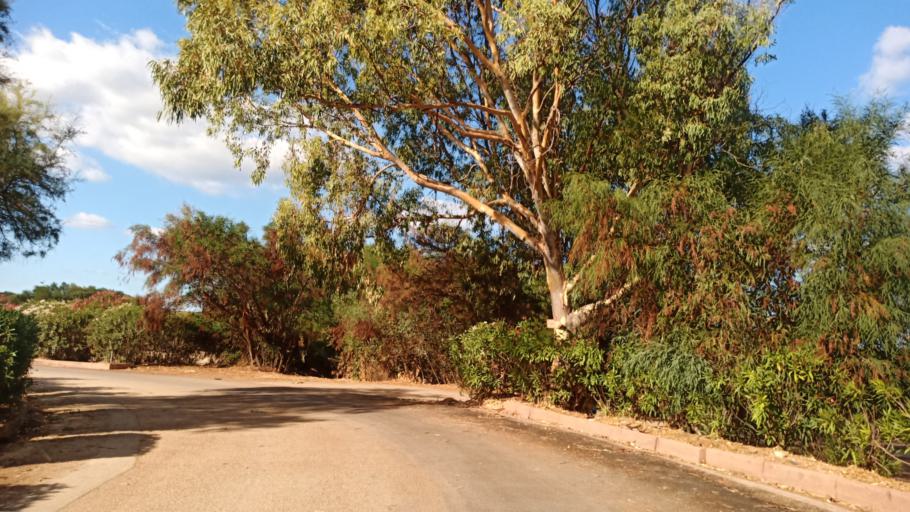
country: IT
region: Sardinia
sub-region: Provincia di Olbia-Tempio
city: Trinita d'Agultu
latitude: 41.0236
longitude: 8.8948
